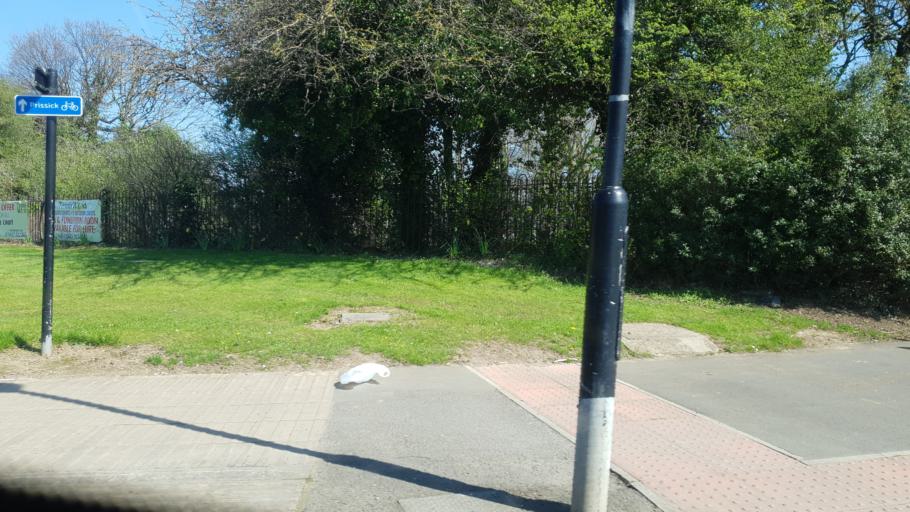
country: GB
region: England
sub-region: Middlesbrough
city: Nunthorpe
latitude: 54.5410
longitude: -1.2109
